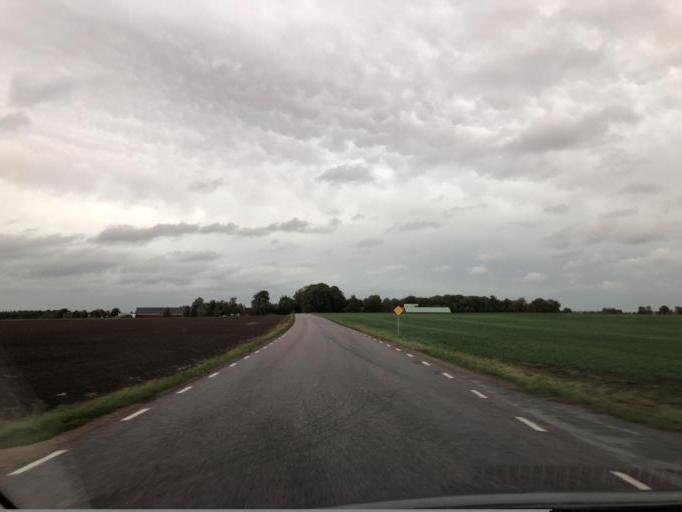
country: SE
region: Skane
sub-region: Kavlinge Kommun
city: Loddekopinge
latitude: 55.7587
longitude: 13.0616
